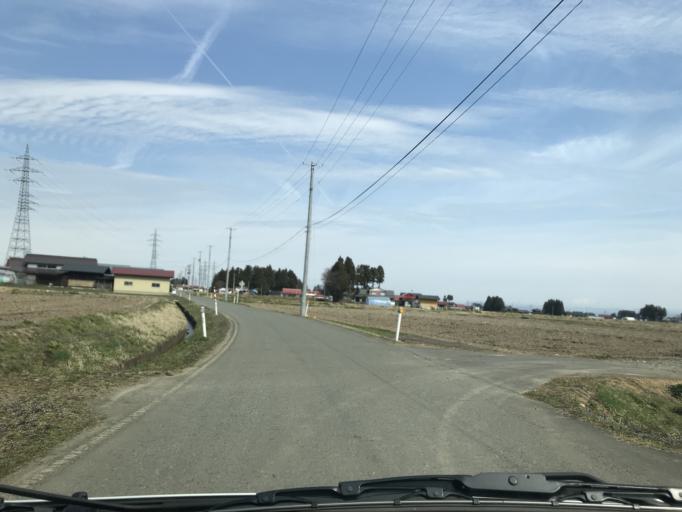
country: JP
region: Iwate
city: Mizusawa
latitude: 39.1181
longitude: 141.0861
